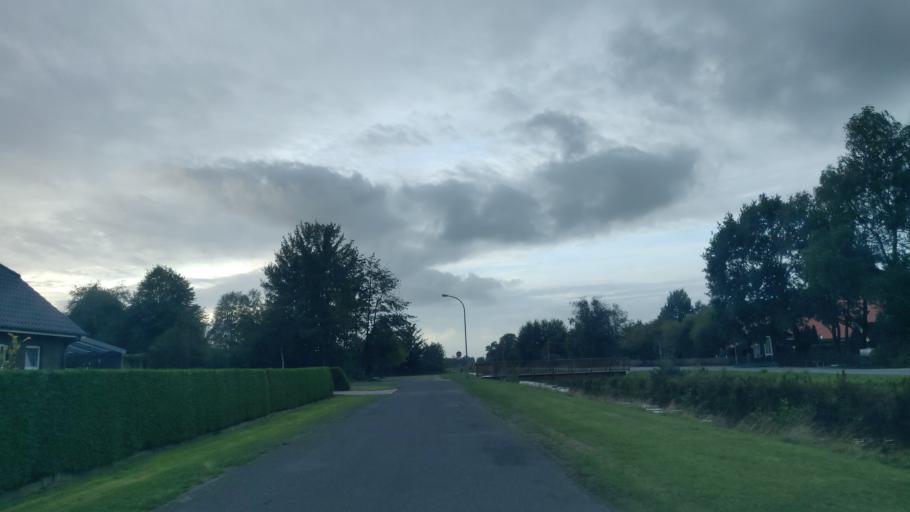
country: DE
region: Lower Saxony
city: Rechtsupweg
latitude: 53.4862
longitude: 7.3960
